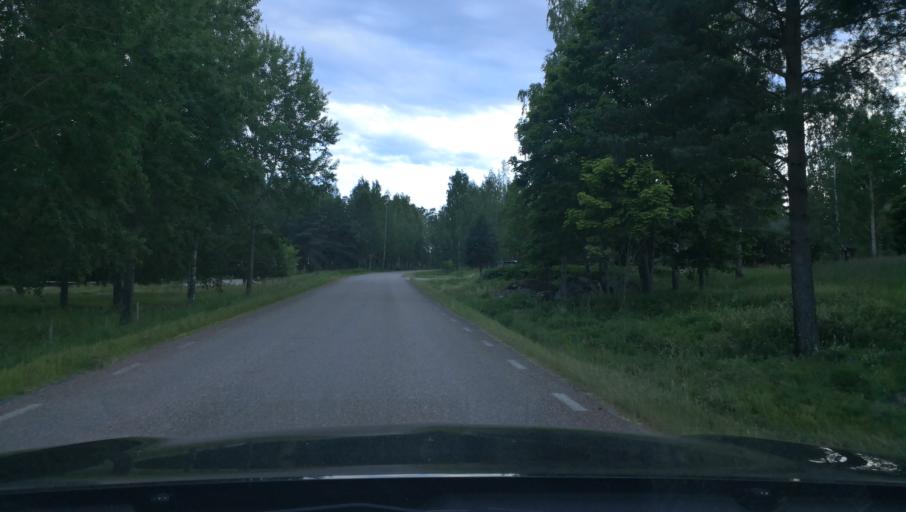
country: SE
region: Dalarna
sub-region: Ludvika Kommun
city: Ludvika
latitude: 60.1192
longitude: 15.2619
